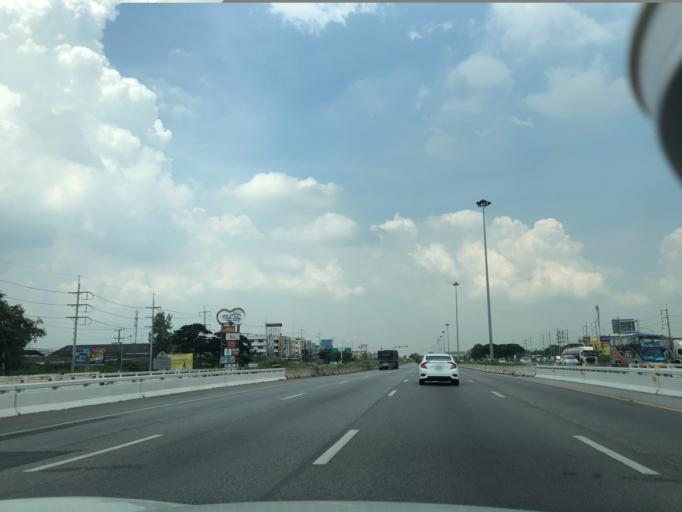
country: TH
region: Phra Nakhon Si Ayutthaya
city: Phra Nakhon Si Ayutthaya
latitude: 14.3451
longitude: 100.6131
